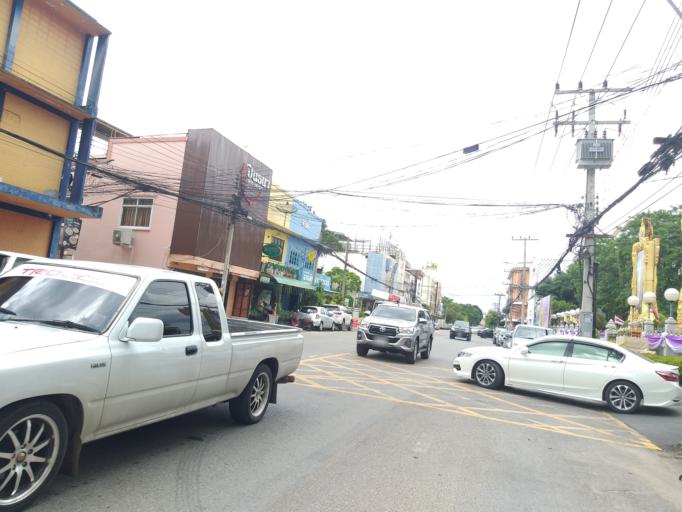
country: TH
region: Nakhon Ratchasima
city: Nakhon Ratchasima
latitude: 14.9741
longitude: 102.0853
